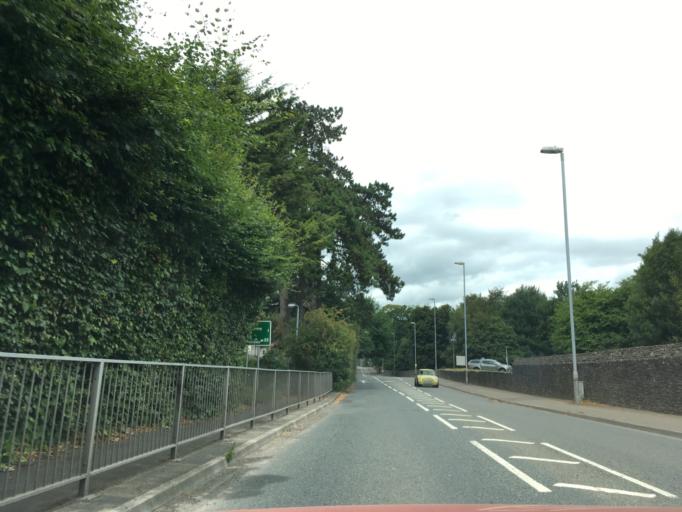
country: GB
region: Wales
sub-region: Monmouthshire
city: Abergavenny
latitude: 51.8130
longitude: -3.0108
